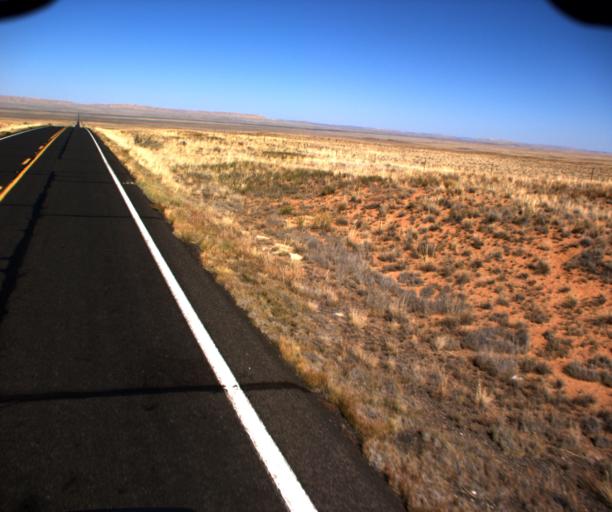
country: US
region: Arizona
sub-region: Navajo County
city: First Mesa
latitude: 35.6410
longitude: -110.4858
